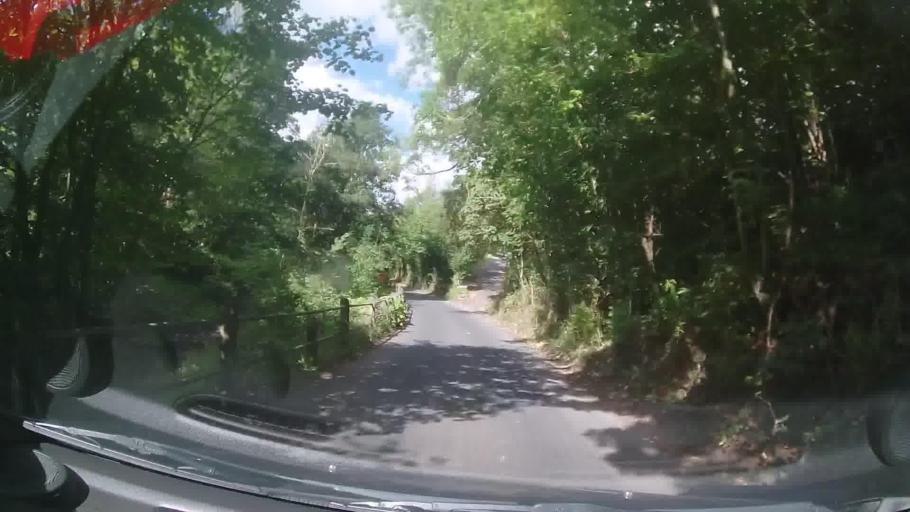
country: GB
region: Wales
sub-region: Merthyr Tydfil County Borough
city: Merthyr Tydfil
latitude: 51.7914
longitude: -3.3636
